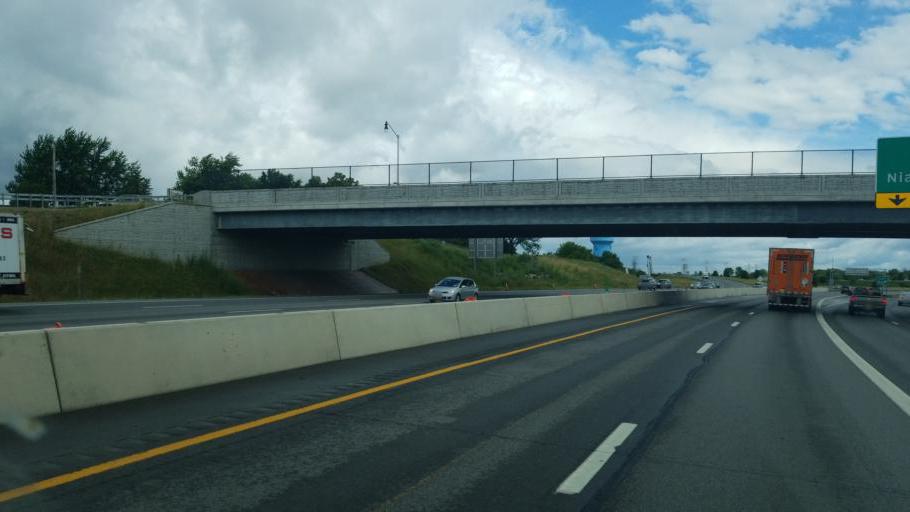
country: US
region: New York
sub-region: Erie County
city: Williamsville
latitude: 42.9446
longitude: -78.7662
